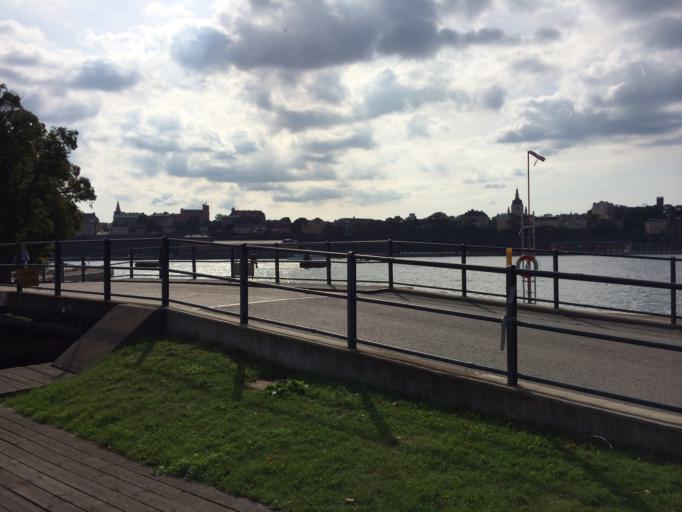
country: SE
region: Stockholm
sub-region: Stockholms Kommun
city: OEstermalm
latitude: 59.3239
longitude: 18.0876
